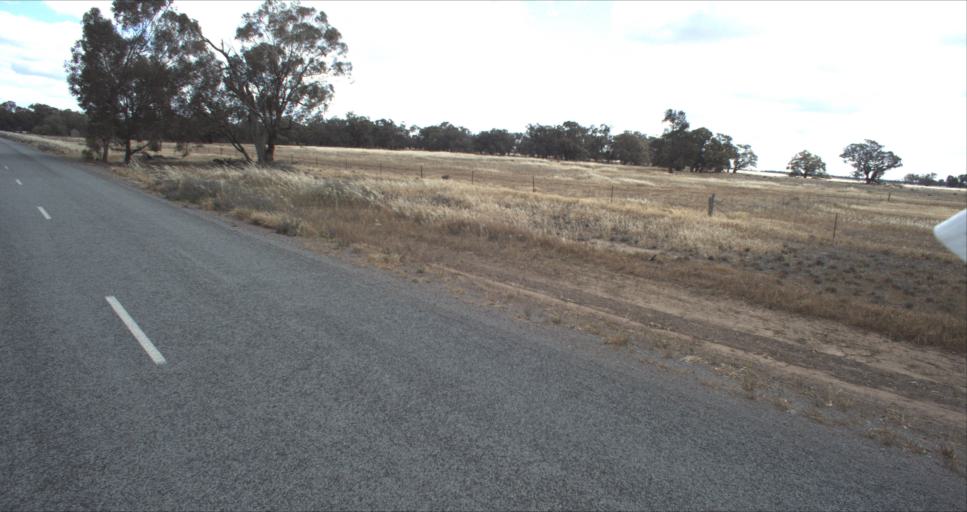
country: AU
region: New South Wales
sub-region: Leeton
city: Leeton
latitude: -34.6873
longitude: 146.3444
